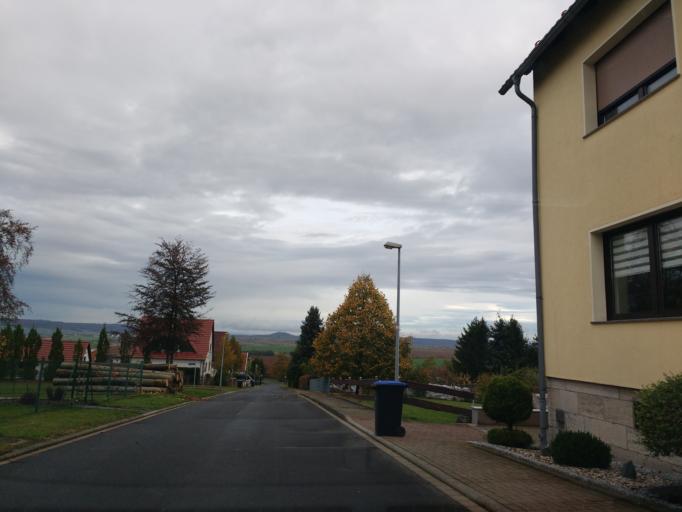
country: DE
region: Thuringia
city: Niederorschel
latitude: 51.3464
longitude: 10.4463
